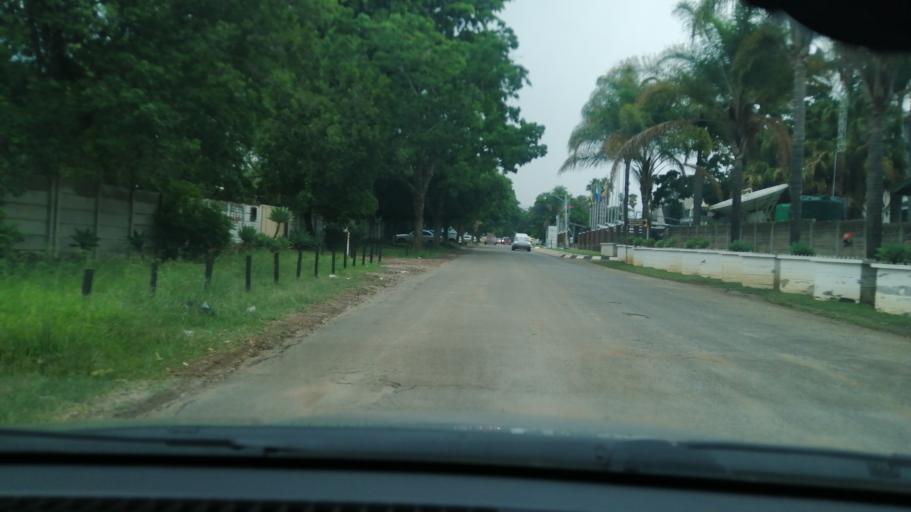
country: ZW
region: Harare
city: Harare
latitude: -17.7992
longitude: 31.0427
